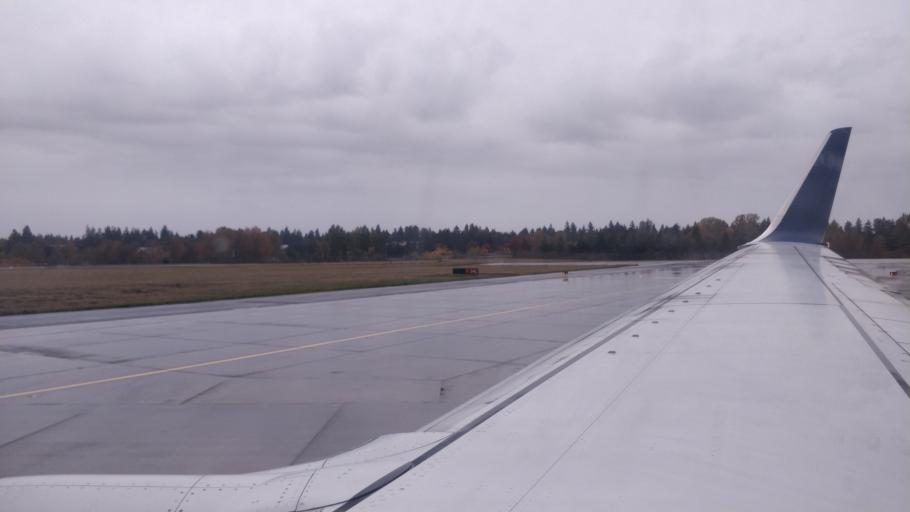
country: US
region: Washington
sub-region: King County
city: SeaTac
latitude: 47.4409
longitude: -122.3156
